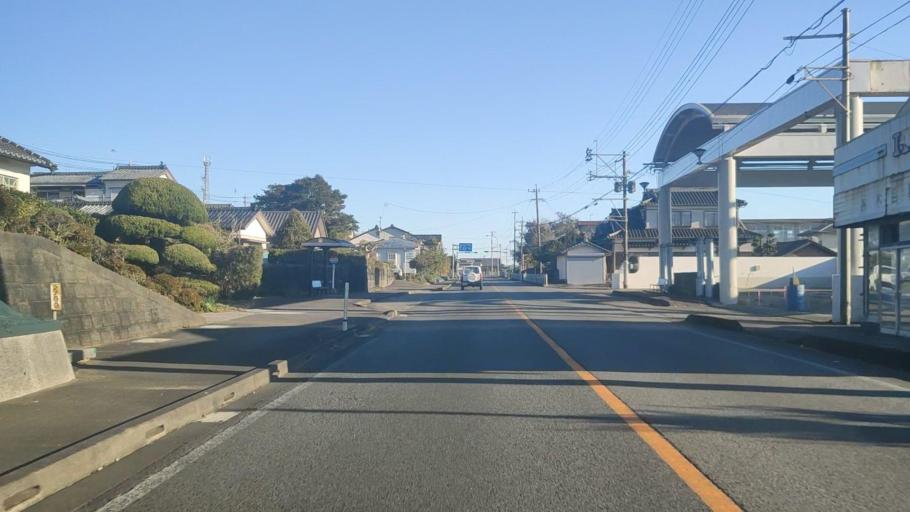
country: JP
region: Miyazaki
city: Nobeoka
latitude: 32.3702
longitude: 131.6293
